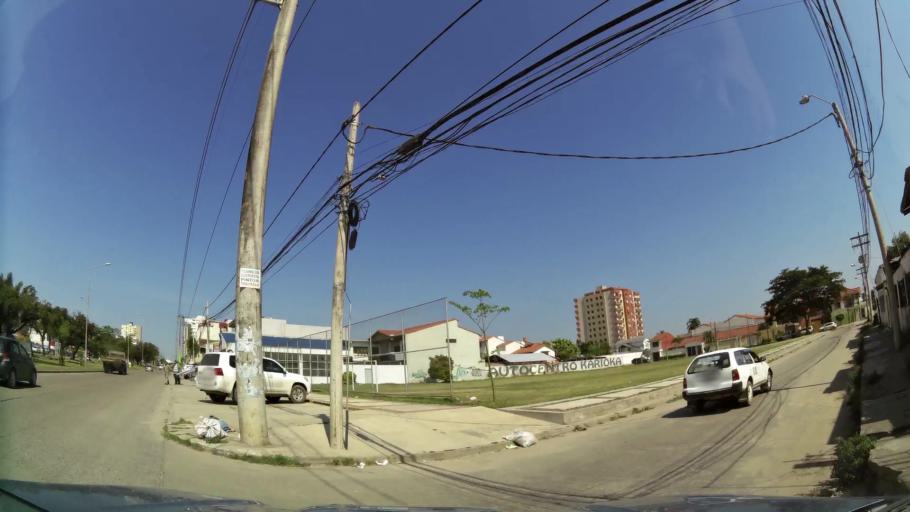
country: BO
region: Santa Cruz
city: Santa Cruz de la Sierra
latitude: -17.7437
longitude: -63.1672
